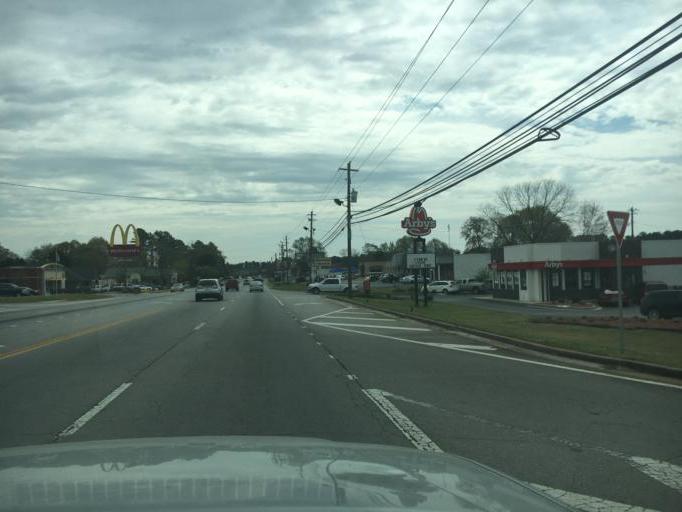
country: US
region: Georgia
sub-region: Stephens County
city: Toccoa
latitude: 34.5697
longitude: -83.3054
